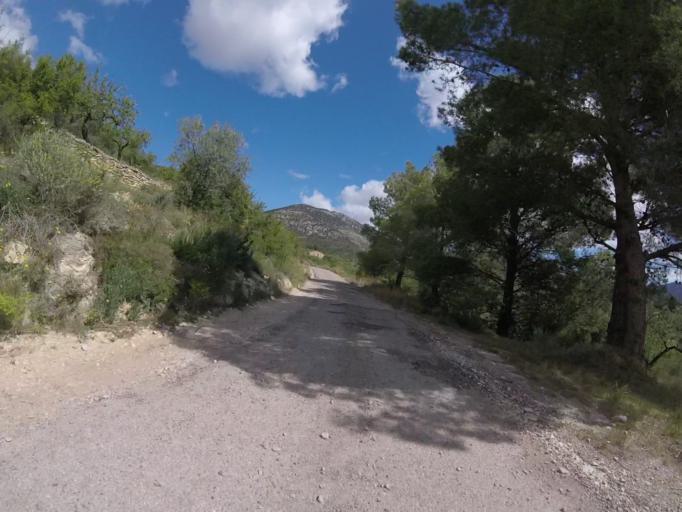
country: ES
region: Valencia
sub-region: Provincia de Castello
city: Sierra-Engarceran
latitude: 40.2727
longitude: -0.0911
